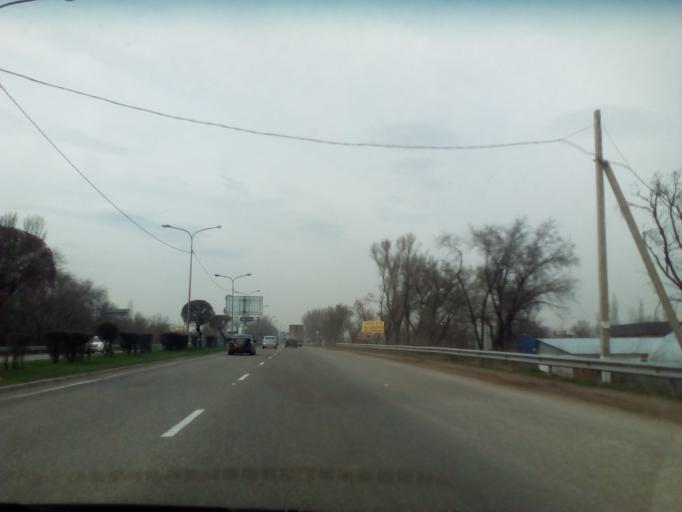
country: KZ
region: Almaty Oblysy
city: Burunday
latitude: 43.2189
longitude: 76.6434
